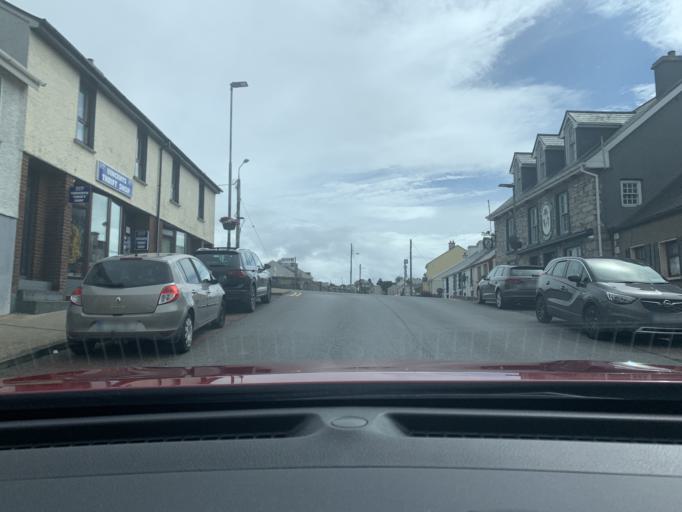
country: IE
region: Ulster
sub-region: County Donegal
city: Dungloe
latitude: 54.9482
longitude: -8.3597
